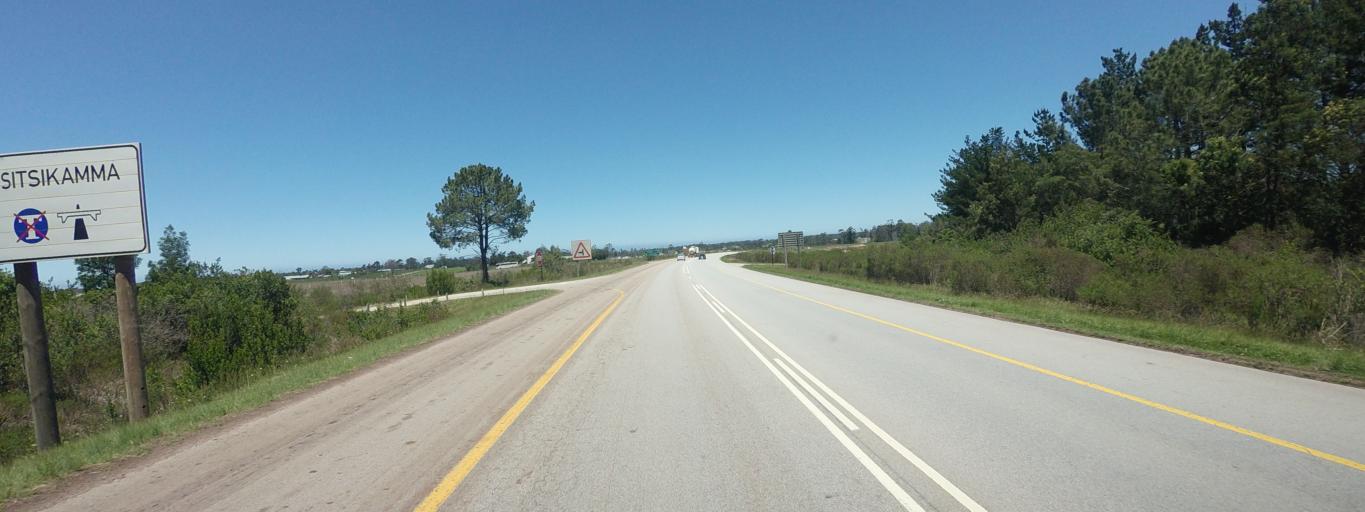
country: ZA
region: Western Cape
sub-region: Eden District Municipality
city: Plettenberg Bay
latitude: -33.9433
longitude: 23.4878
